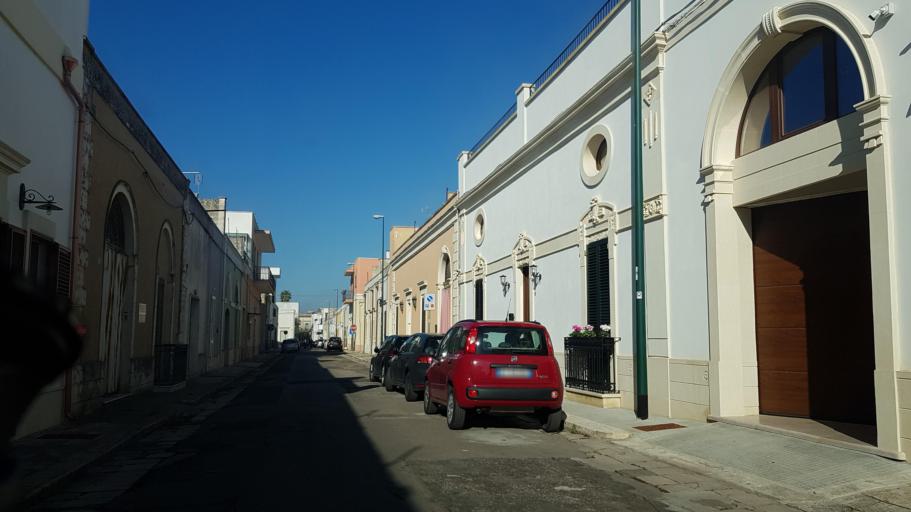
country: IT
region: Apulia
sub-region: Provincia di Lecce
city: Campi Salentina
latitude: 40.3961
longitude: 18.0202
